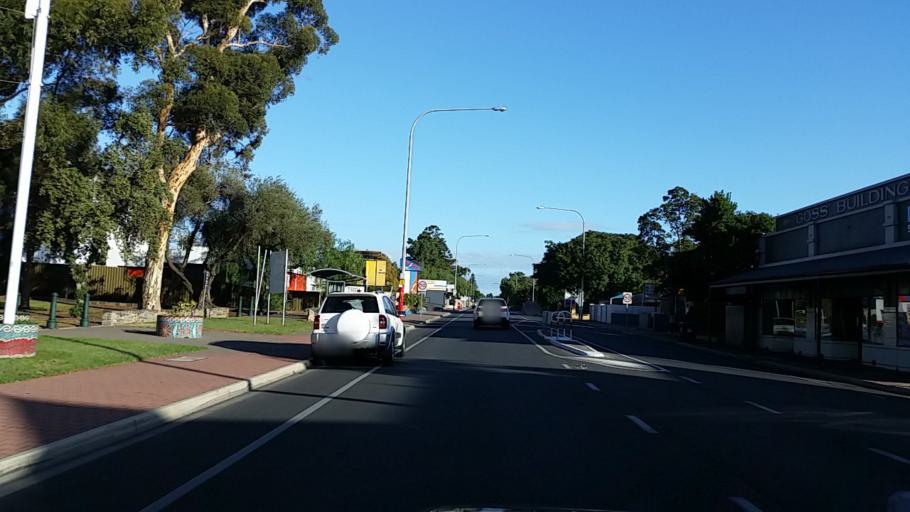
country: AU
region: South Australia
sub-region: Prospect
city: Prospect
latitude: -34.8925
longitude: 138.5944
